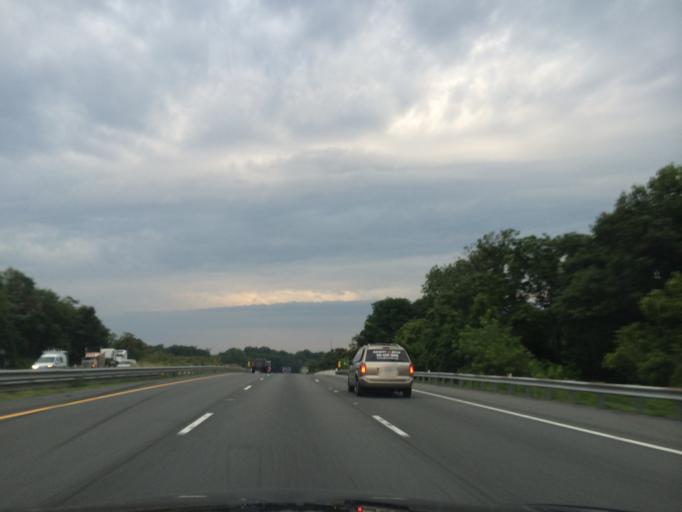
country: US
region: Maryland
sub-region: Carroll County
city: Mount Airy
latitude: 39.3667
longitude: -77.1925
